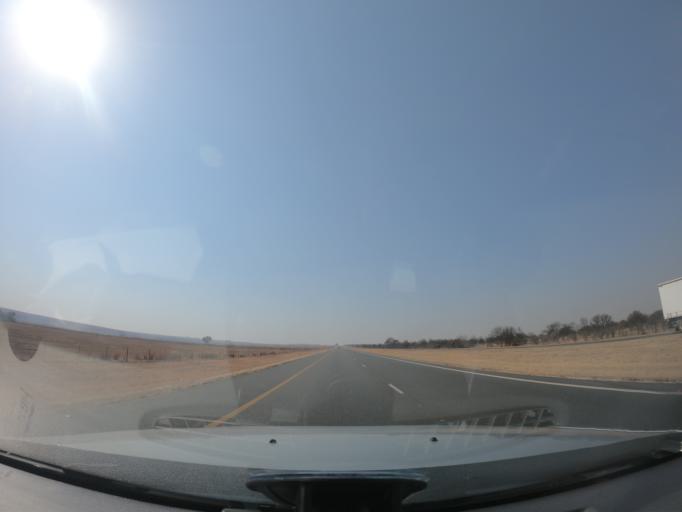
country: ZA
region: Mpumalanga
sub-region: Nkangala District Municipality
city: Witbank
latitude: -25.8696
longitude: 29.0233
